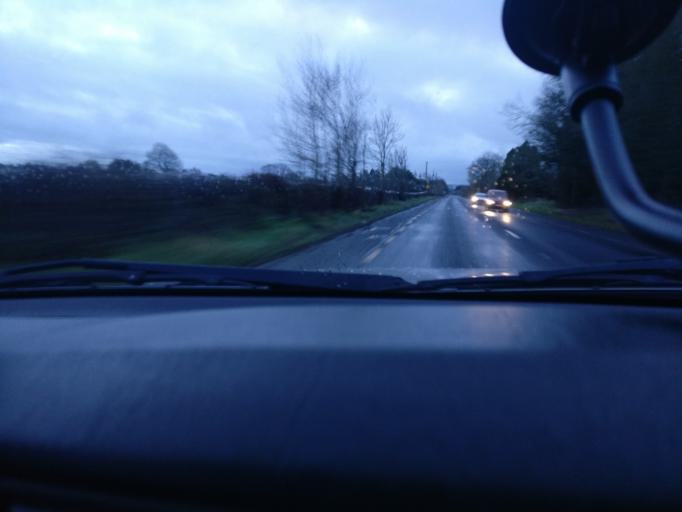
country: IE
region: Connaught
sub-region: County Galway
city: Loughrea
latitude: 53.2468
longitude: -8.4462
